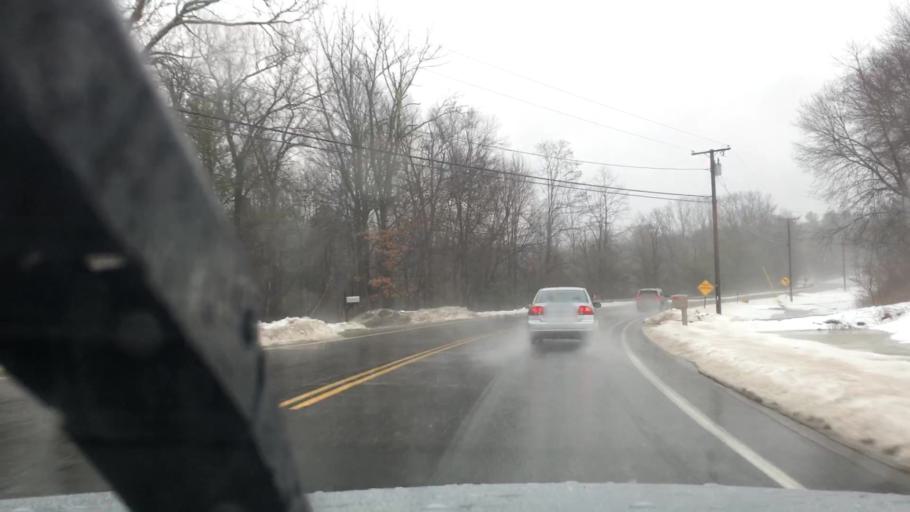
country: US
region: Massachusetts
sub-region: Hampshire County
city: Granby
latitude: 42.2471
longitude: -72.4784
